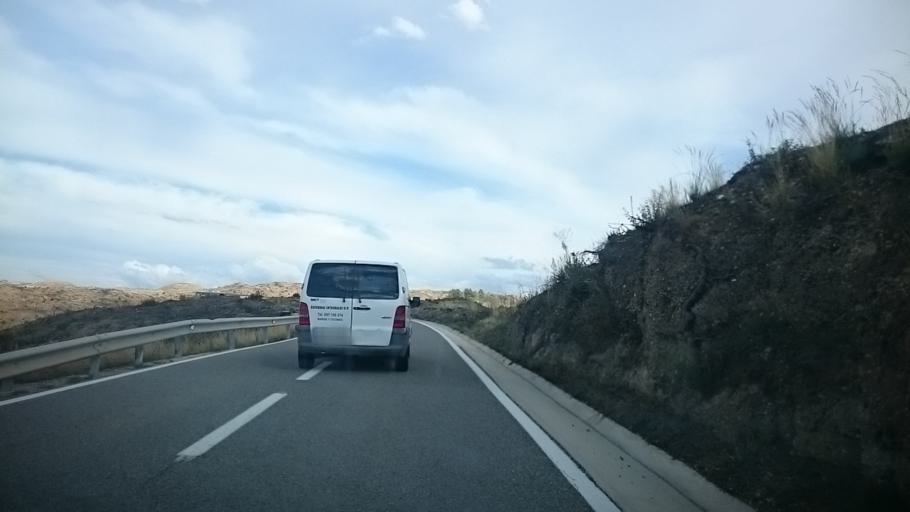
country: ES
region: Catalonia
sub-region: Provincia de Barcelona
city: Castelloli
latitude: 41.6269
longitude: 1.6763
